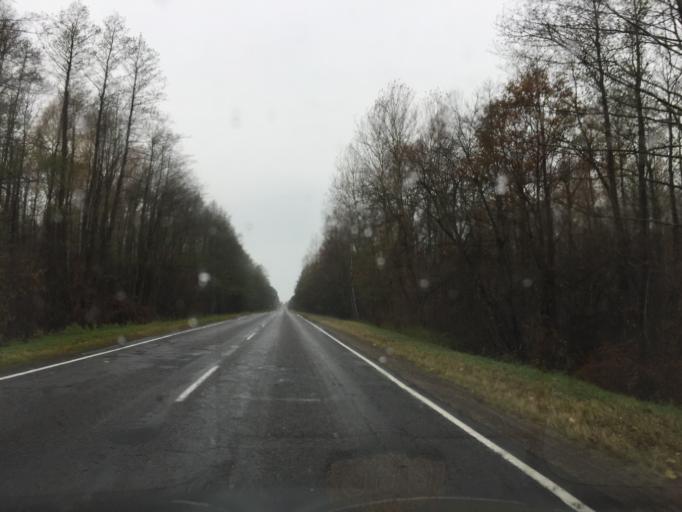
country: BY
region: Gomel
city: Karma
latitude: 53.3173
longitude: 30.7557
